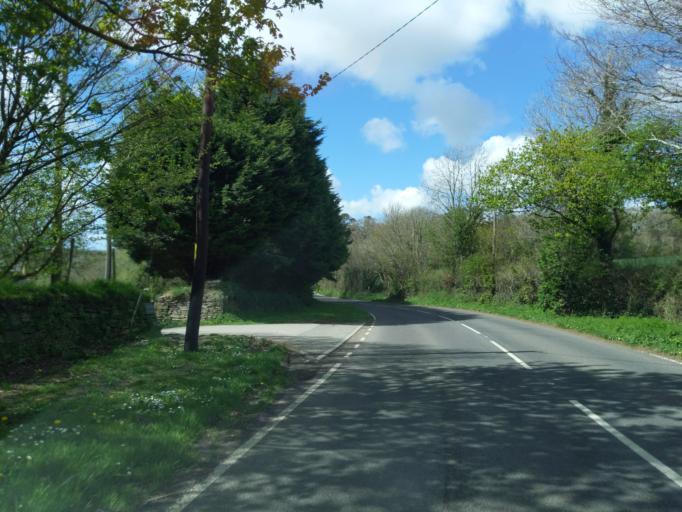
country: GB
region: England
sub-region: Cornwall
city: Bodmin
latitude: 50.4955
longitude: -4.7693
